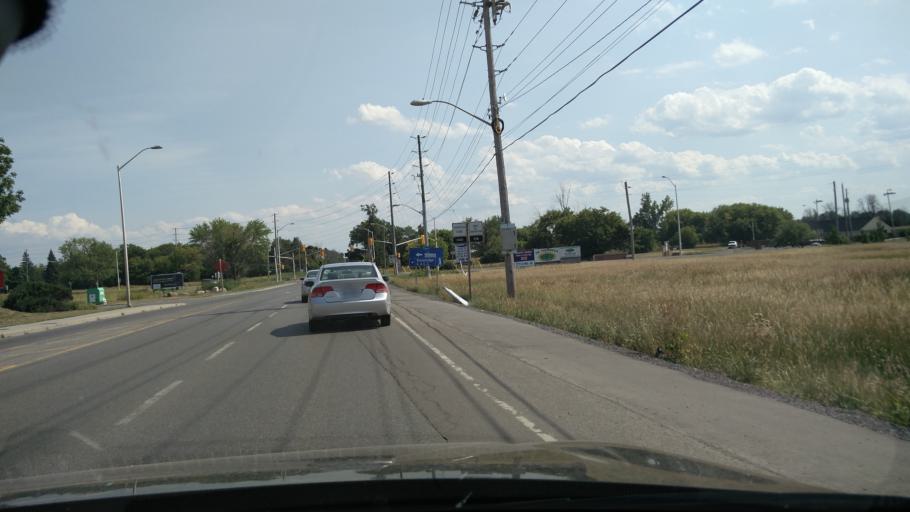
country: CA
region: Ontario
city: Bells Corners
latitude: 45.2677
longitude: -75.7449
